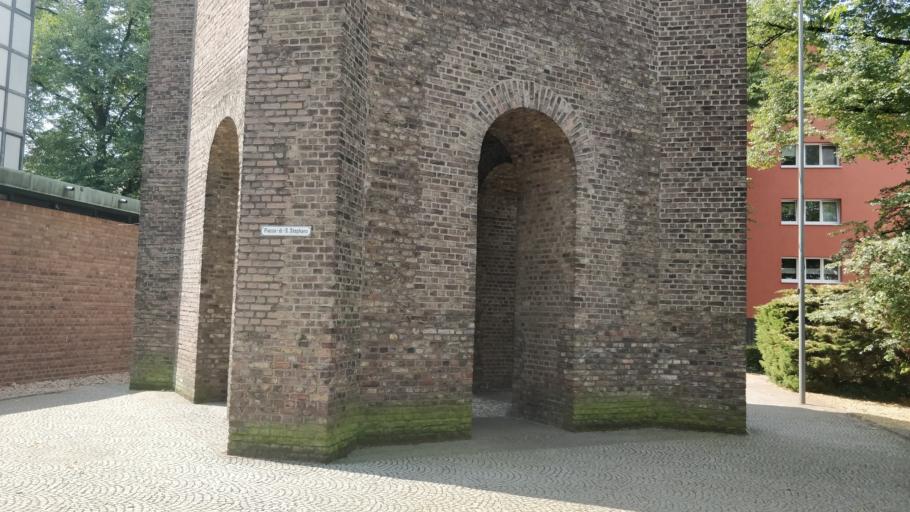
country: DE
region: North Rhine-Westphalia
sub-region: Regierungsbezirk Koln
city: Neustadt/Sued
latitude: 50.9272
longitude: 6.9136
